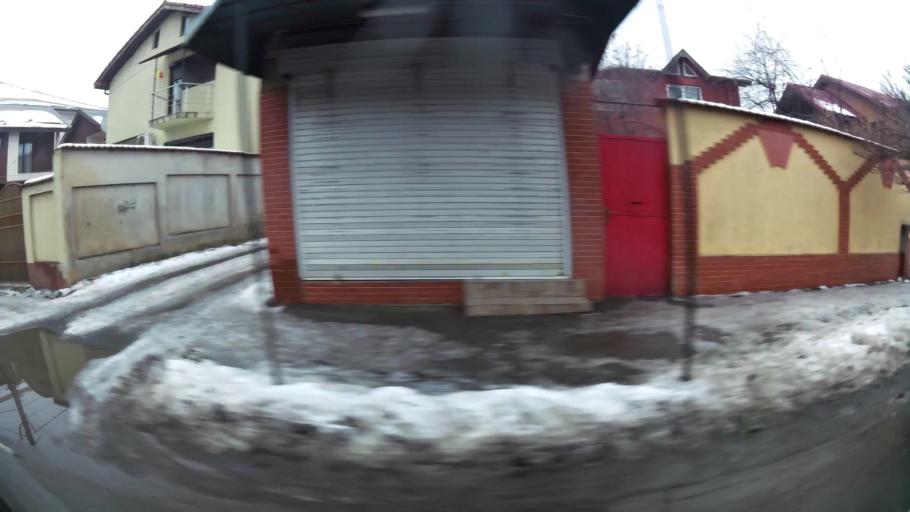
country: RO
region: Ilfov
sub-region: Comuna Chiajna
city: Rosu
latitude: 44.4500
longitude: 26.0094
